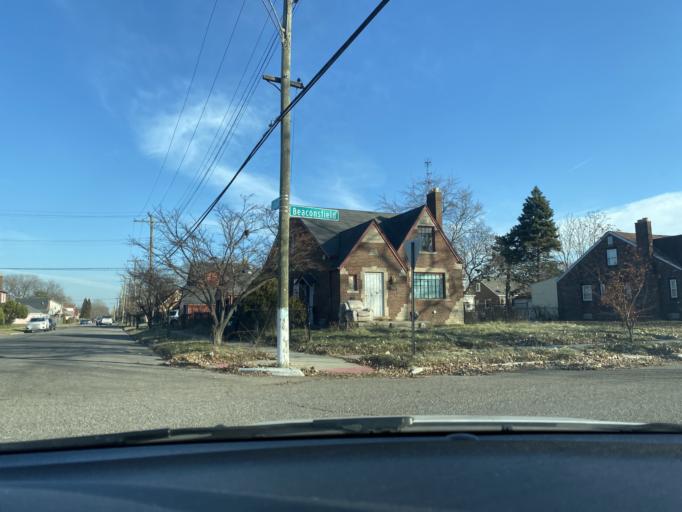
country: US
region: Michigan
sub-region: Wayne County
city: Grosse Pointe Park
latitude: 42.4053
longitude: -82.9542
